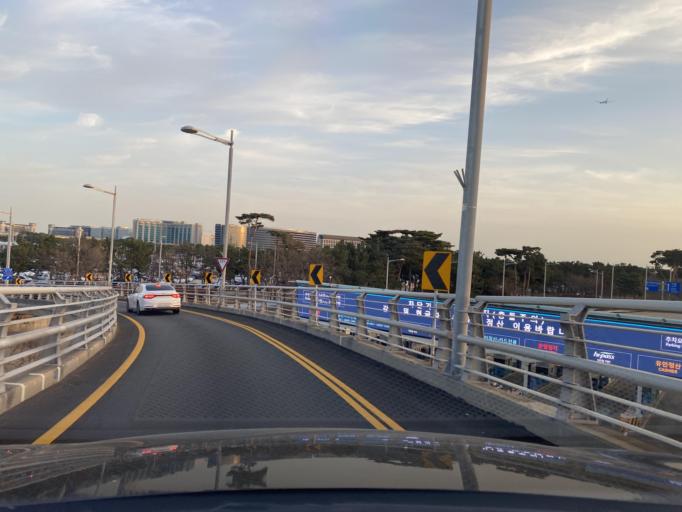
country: KR
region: Incheon
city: Incheon
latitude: 37.4452
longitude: 126.4498
